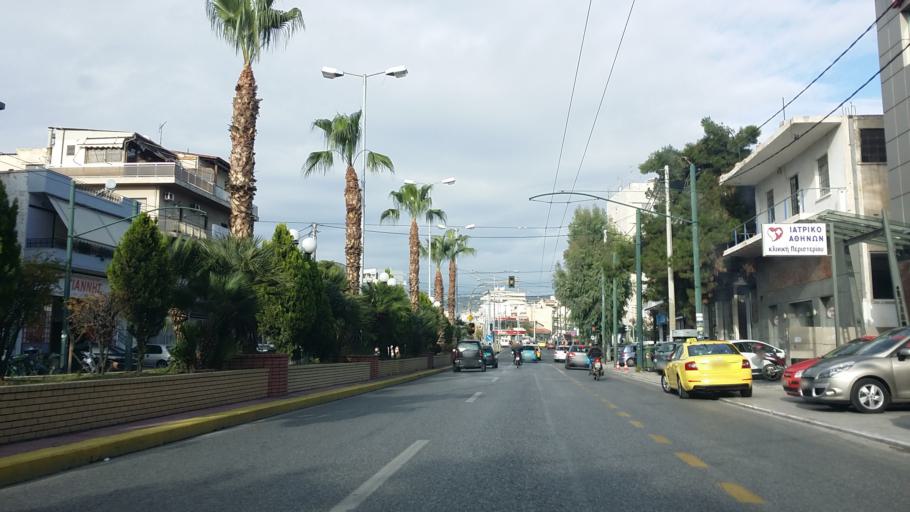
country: GR
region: Attica
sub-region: Nomarchia Athinas
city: Peristeri
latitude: 38.0052
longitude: 23.7010
